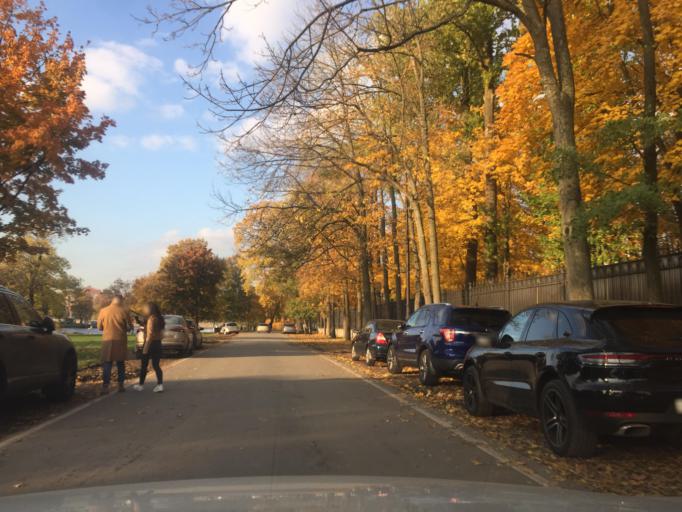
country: RU
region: St.-Petersburg
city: Novaya Derevnya
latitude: 59.9781
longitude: 30.2749
